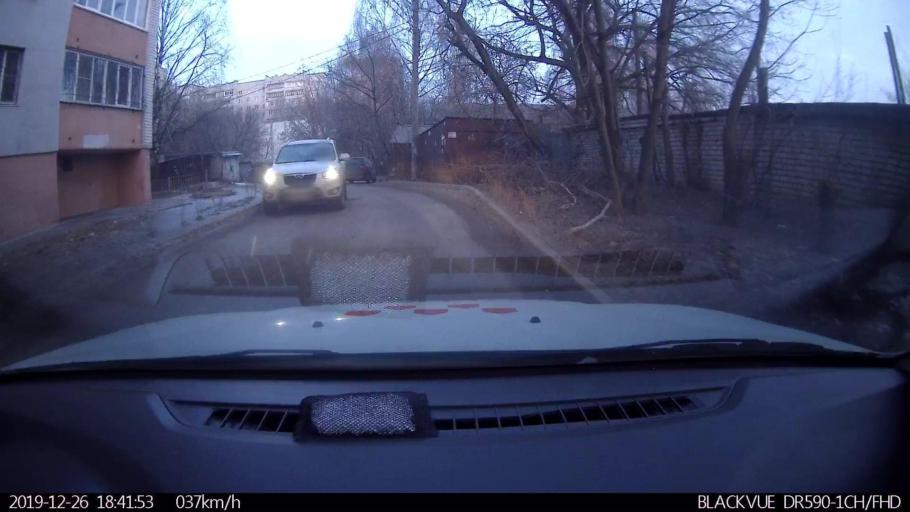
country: RU
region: Nizjnij Novgorod
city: Nizhniy Novgorod
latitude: 56.3173
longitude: 44.0335
